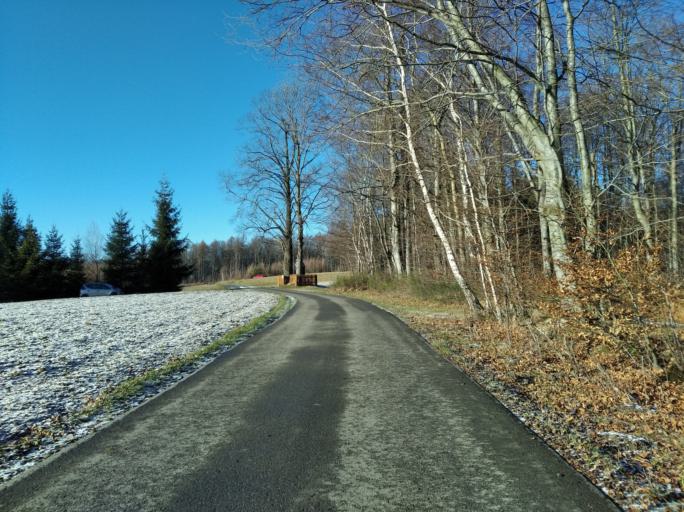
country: PL
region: Subcarpathian Voivodeship
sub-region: Powiat ropczycko-sedziszowski
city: Iwierzyce
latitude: 49.9686
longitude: 21.7331
